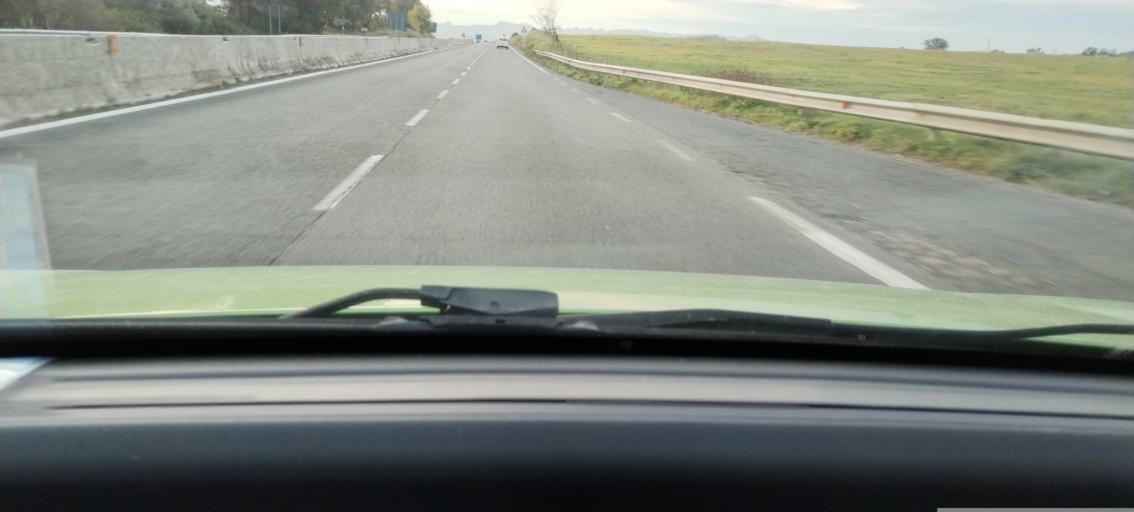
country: IT
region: Latium
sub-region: Provincia di Viterbo
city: Monterosi
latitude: 42.1775
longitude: 12.3235
